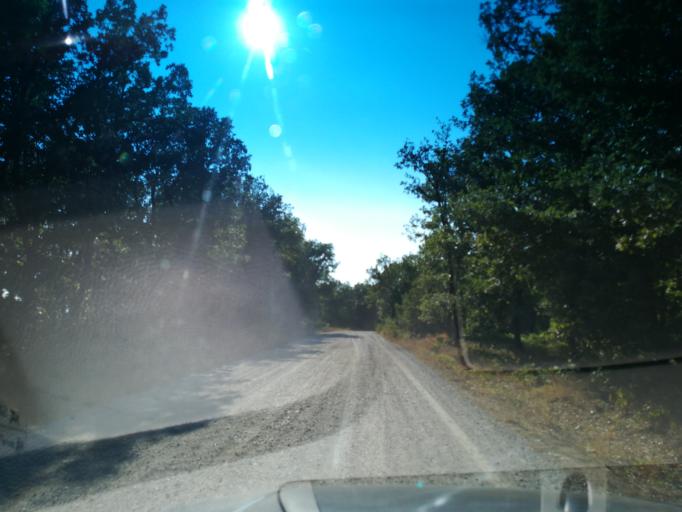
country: BG
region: Khaskovo
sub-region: Obshtina Mineralni Bani
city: Mineralni Bani
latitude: 41.9716
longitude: 25.3220
